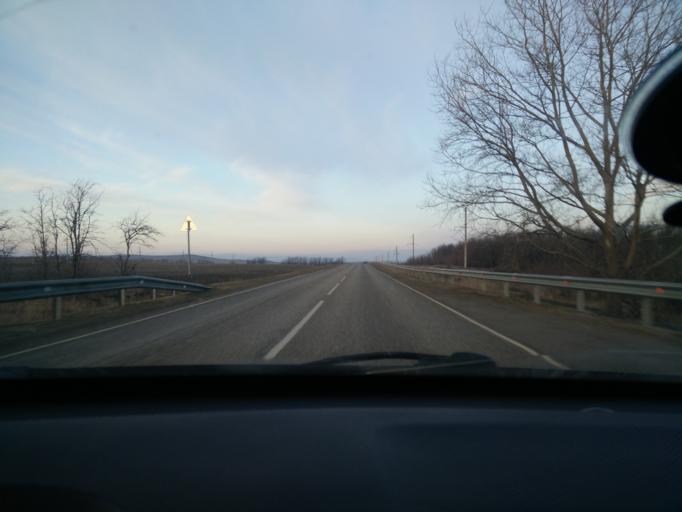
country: RU
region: Stavropol'skiy
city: Tatarka
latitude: 44.9965
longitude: 41.7478
